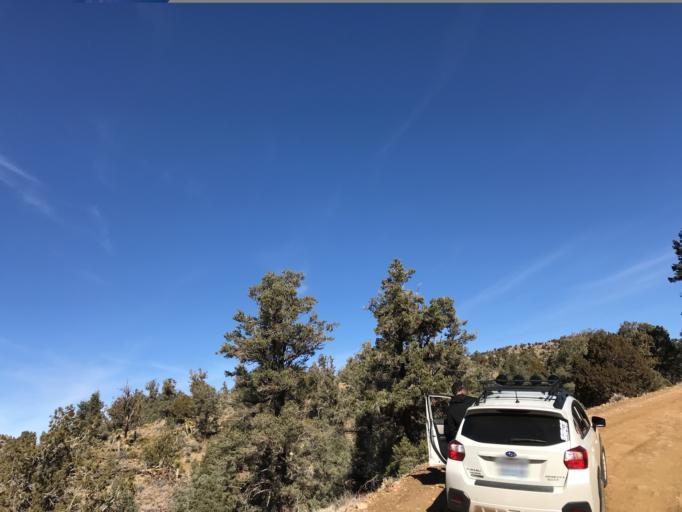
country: US
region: California
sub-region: San Bernardino County
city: Big Bear City
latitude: 34.2567
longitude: -116.7437
